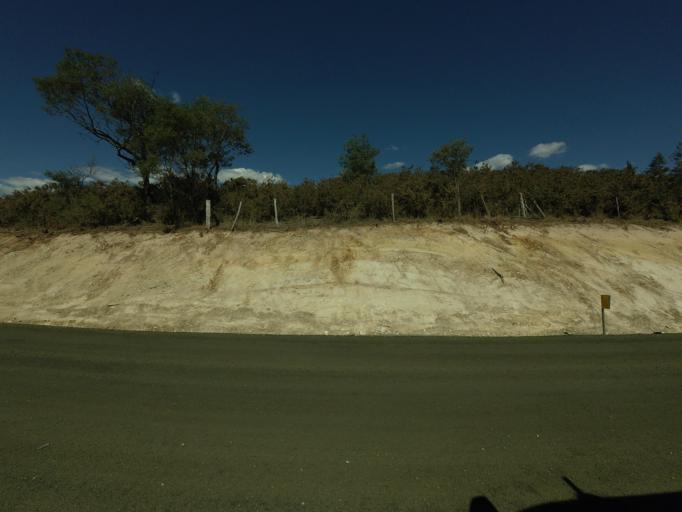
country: AU
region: Tasmania
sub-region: Break O'Day
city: St Helens
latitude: -41.6519
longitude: 147.9257
